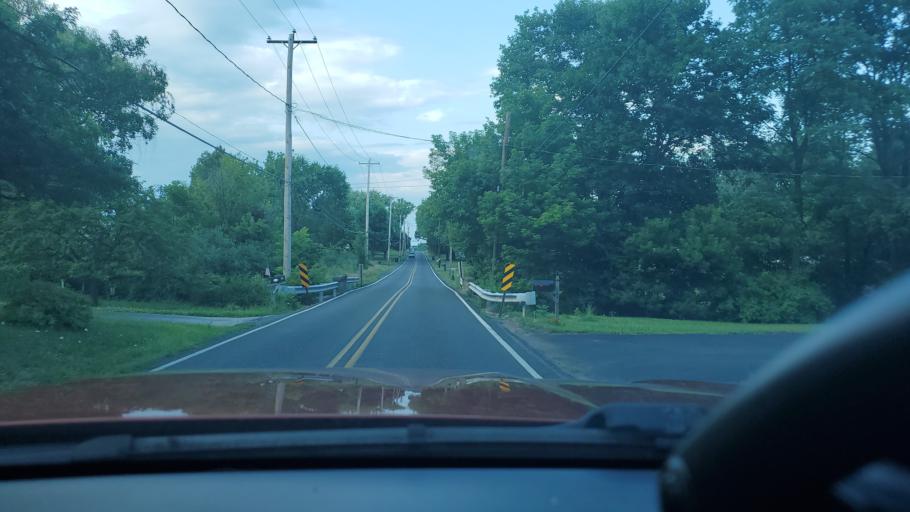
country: US
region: Pennsylvania
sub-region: Montgomery County
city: Limerick
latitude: 40.2272
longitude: -75.5136
